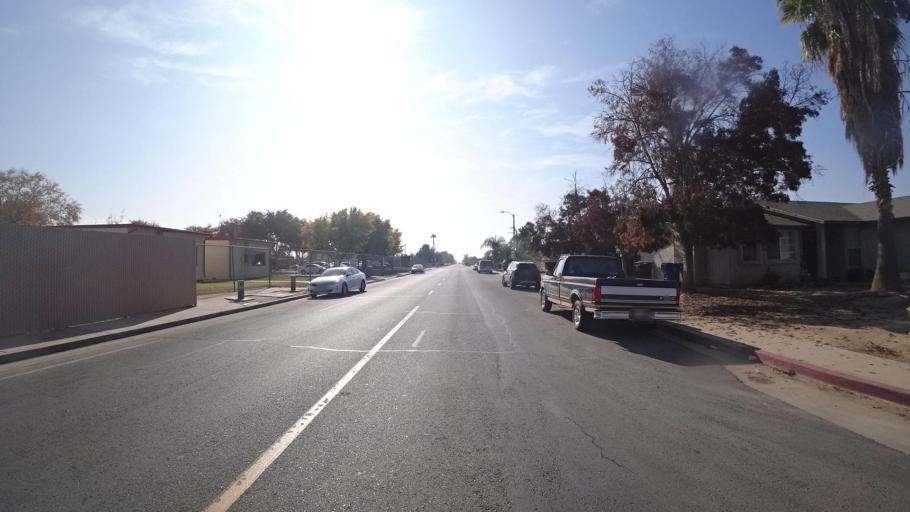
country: US
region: California
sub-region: Kern County
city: McFarland
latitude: 35.6828
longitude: -119.2232
